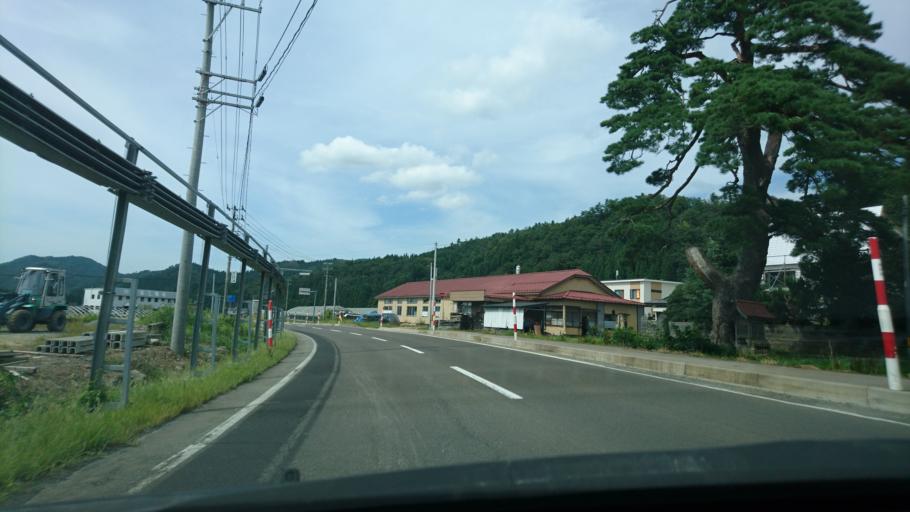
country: JP
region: Akita
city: Yuzawa
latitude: 39.1933
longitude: 140.6180
